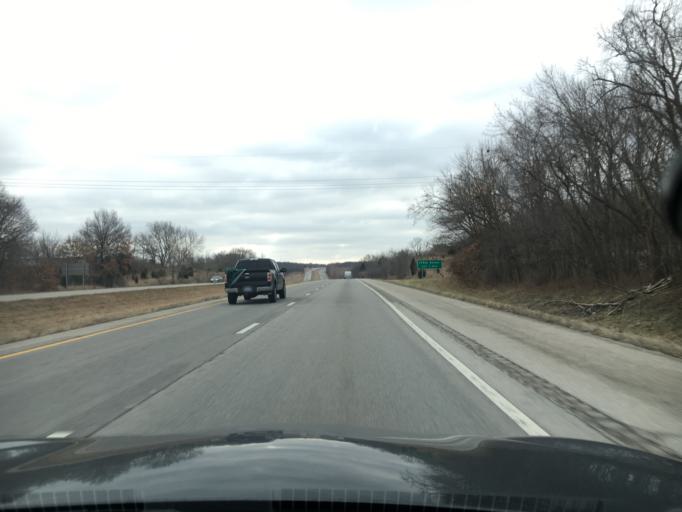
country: US
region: Missouri
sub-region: Cass County
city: Belton
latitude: 38.8195
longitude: -94.6763
